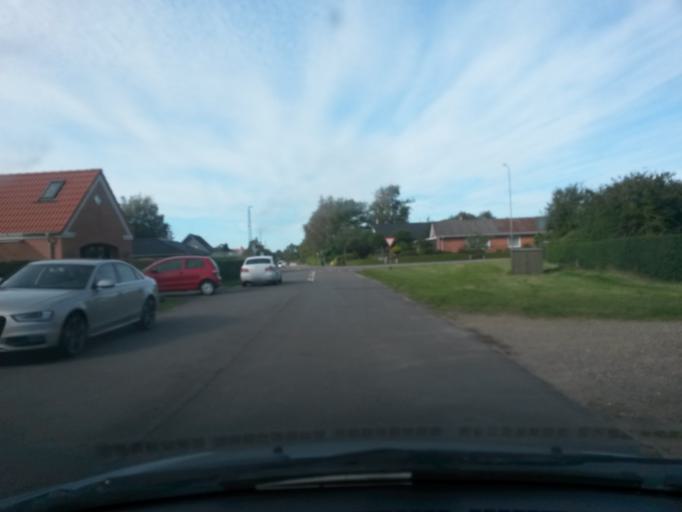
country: DK
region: Central Jutland
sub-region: Silkeborg Kommune
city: Kjellerup
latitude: 56.2778
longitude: 9.4375
